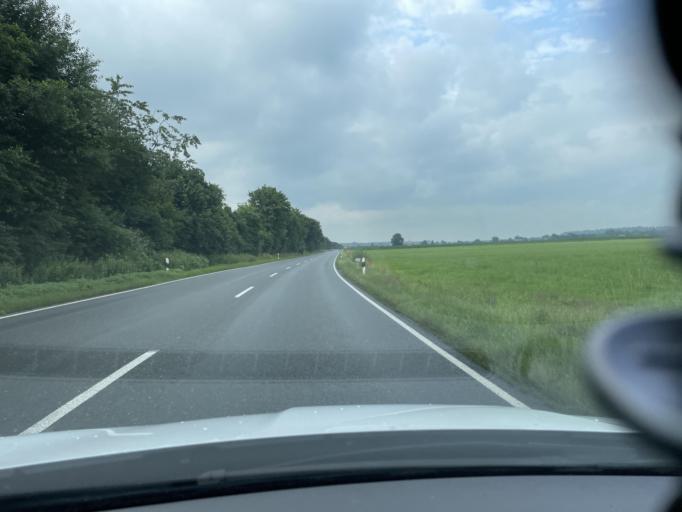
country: DE
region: Bavaria
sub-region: Upper Bavaria
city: Schechen
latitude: 47.9417
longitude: 12.1329
